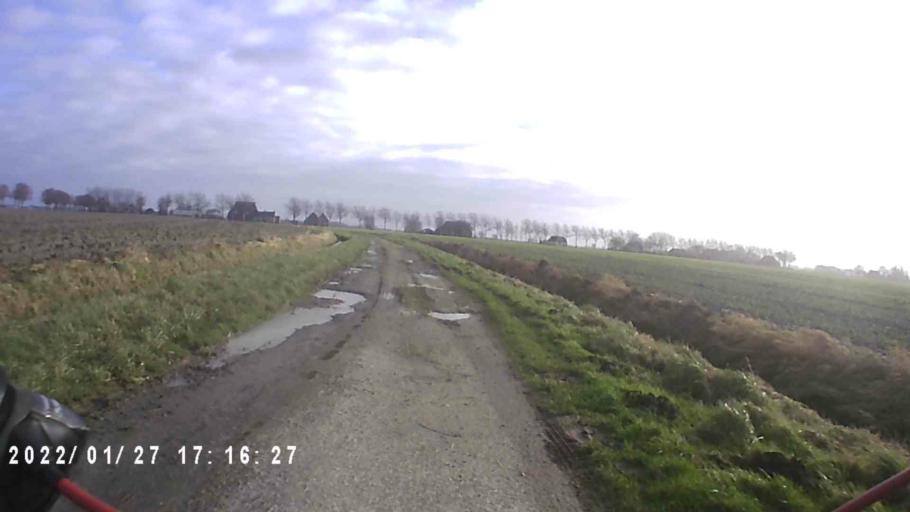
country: NL
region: Friesland
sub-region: Gemeente Dongeradeel
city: Anjum
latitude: 53.3910
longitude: 6.0978
